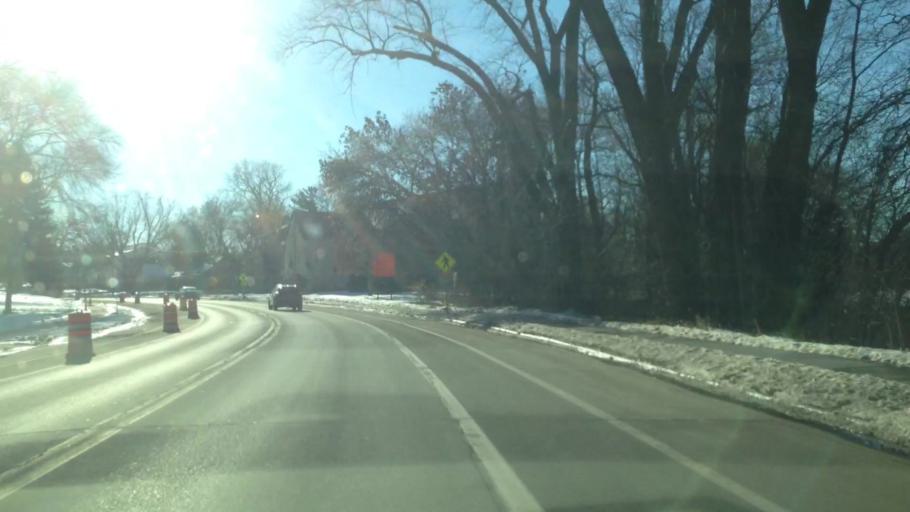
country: US
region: Minnesota
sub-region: Hennepin County
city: Richfield
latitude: 44.8989
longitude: -93.2672
